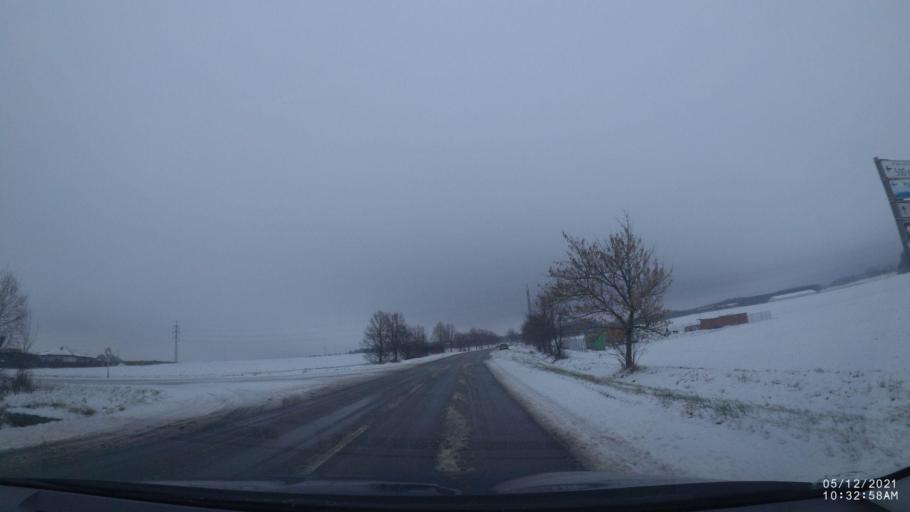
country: CZ
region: Kralovehradecky
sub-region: Okres Rychnov nad Kneznou
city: Rychnov nad Kneznou
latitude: 50.1633
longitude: 16.2921
